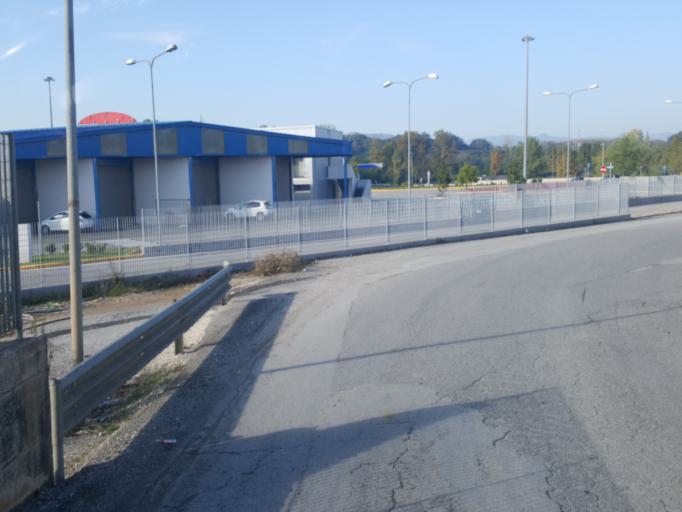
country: IT
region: Latium
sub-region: Citta metropolitana di Roma Capitale
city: Colleferro
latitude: 41.7545
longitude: 12.9886
